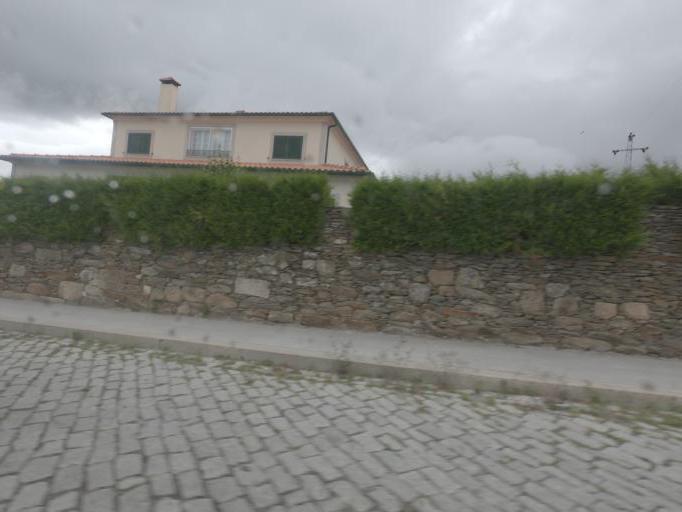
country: PT
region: Vila Real
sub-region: Sabrosa
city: Sabrosa
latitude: 41.2640
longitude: -7.5024
